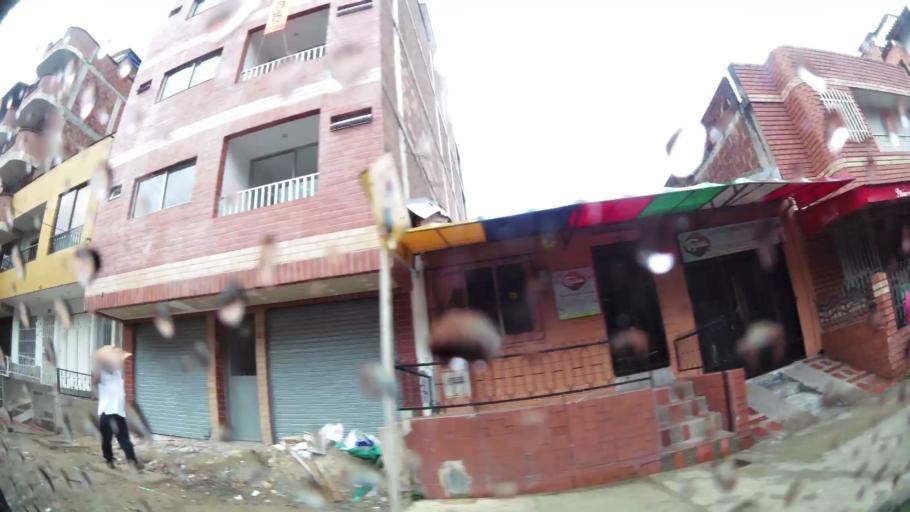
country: CO
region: Antioquia
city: Itagui
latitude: 6.1829
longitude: -75.5965
